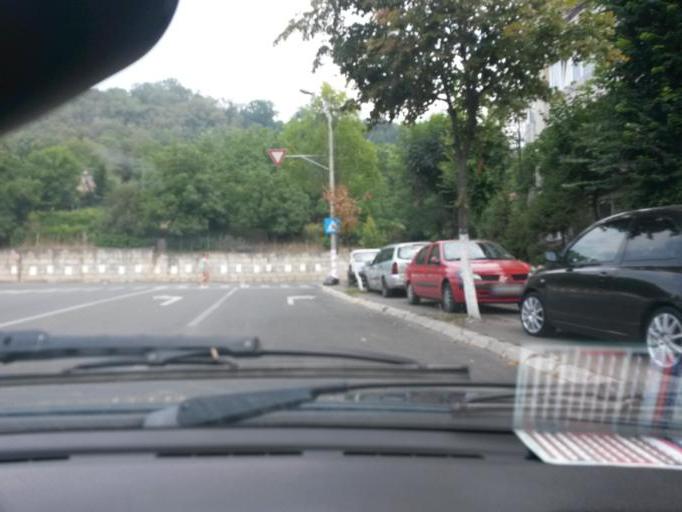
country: RO
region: Mures
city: Targu-Mures
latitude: 46.5393
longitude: 24.5847
